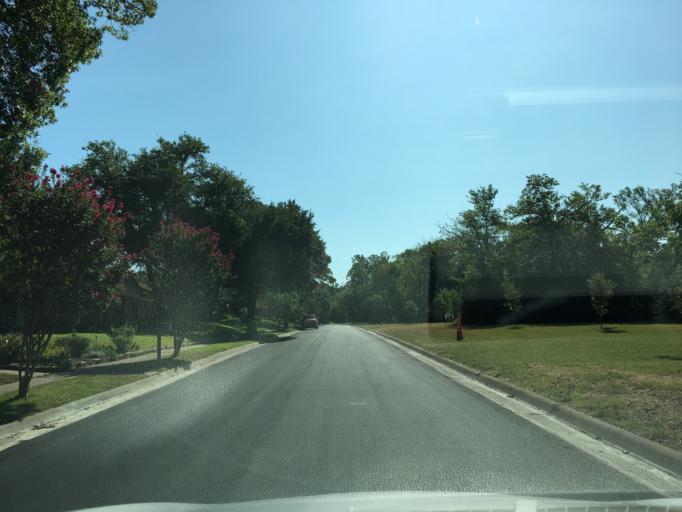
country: US
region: Texas
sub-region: Dallas County
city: Garland
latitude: 32.8545
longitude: -96.6980
